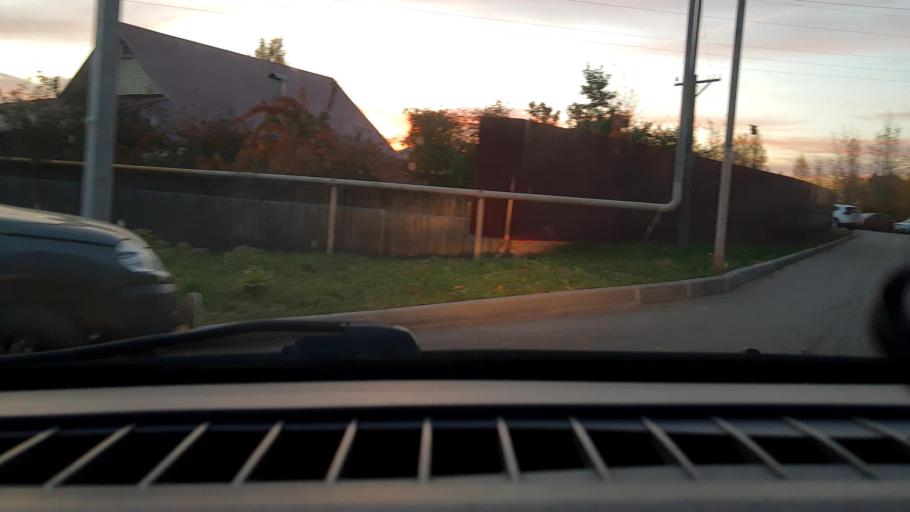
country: RU
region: Nizjnij Novgorod
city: Gorbatovka
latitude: 56.3786
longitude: 43.7974
